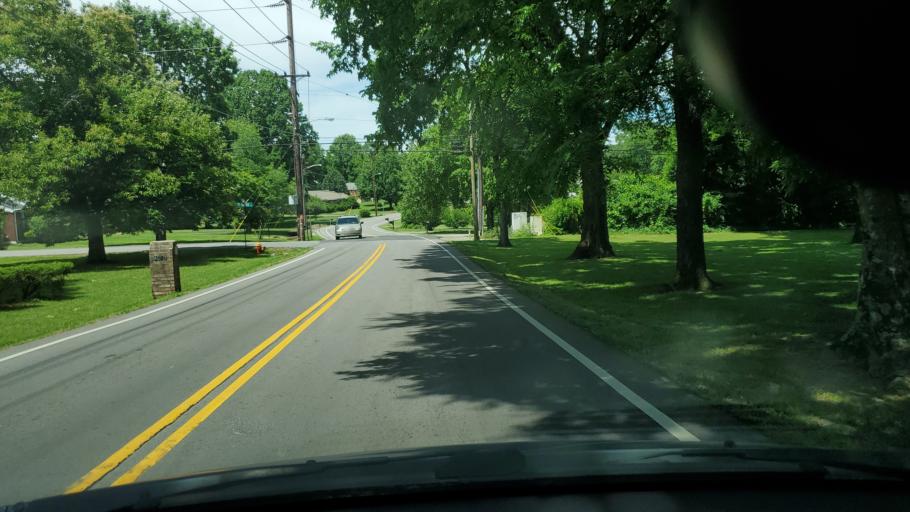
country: US
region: Tennessee
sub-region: Davidson County
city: Nashville
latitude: 36.2274
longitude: -86.7334
